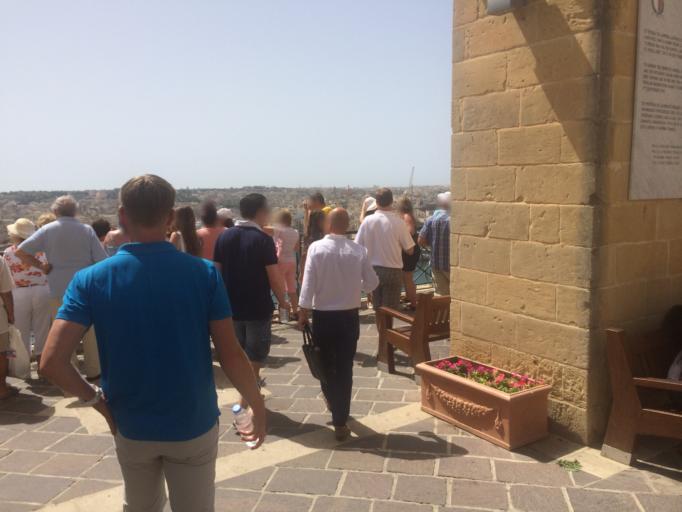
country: MT
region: Il-Furjana
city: Floriana
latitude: 35.8949
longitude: 14.5123
